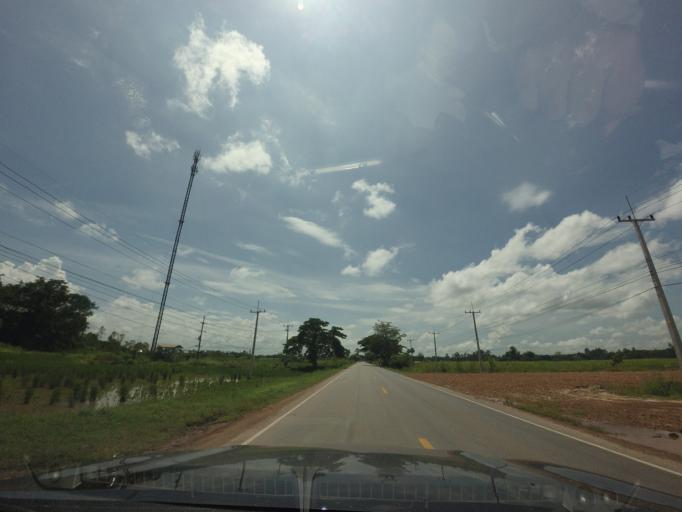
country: TH
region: Nong Khai
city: Pho Tak
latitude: 17.7678
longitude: 102.3967
